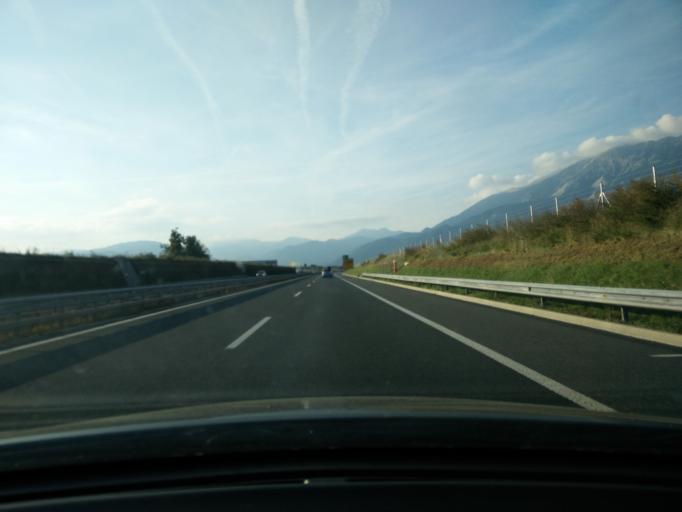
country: SI
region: Radovljica
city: Lesce
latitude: 46.3630
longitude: 14.1657
